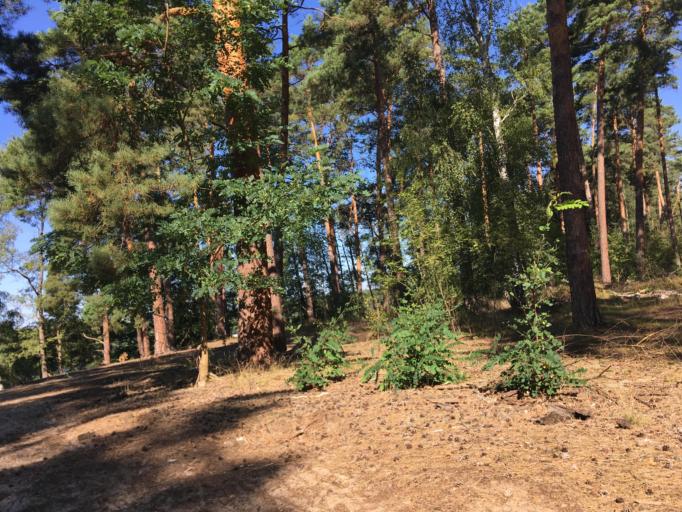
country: DE
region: Brandenburg
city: Gross Koris
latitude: 52.2141
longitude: 13.7538
